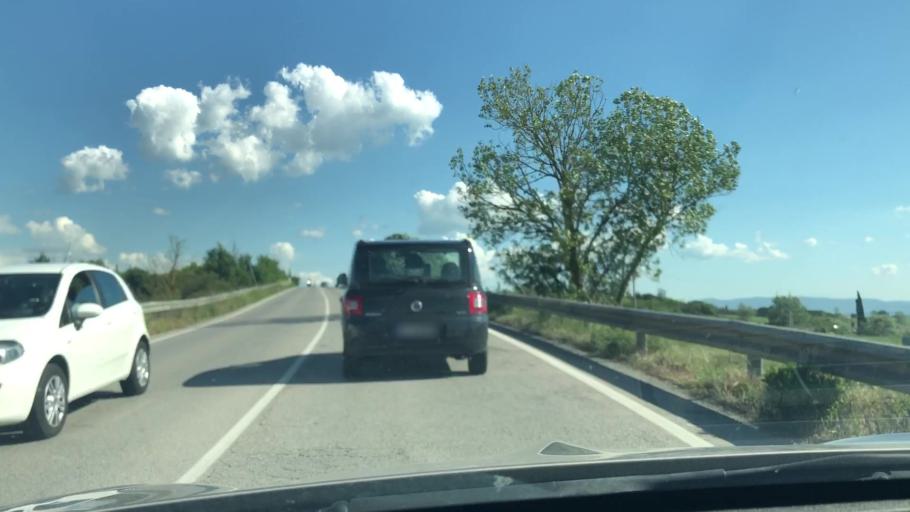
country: IT
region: Tuscany
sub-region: Province of Pisa
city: Il Romito
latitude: 43.6525
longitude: 10.6552
